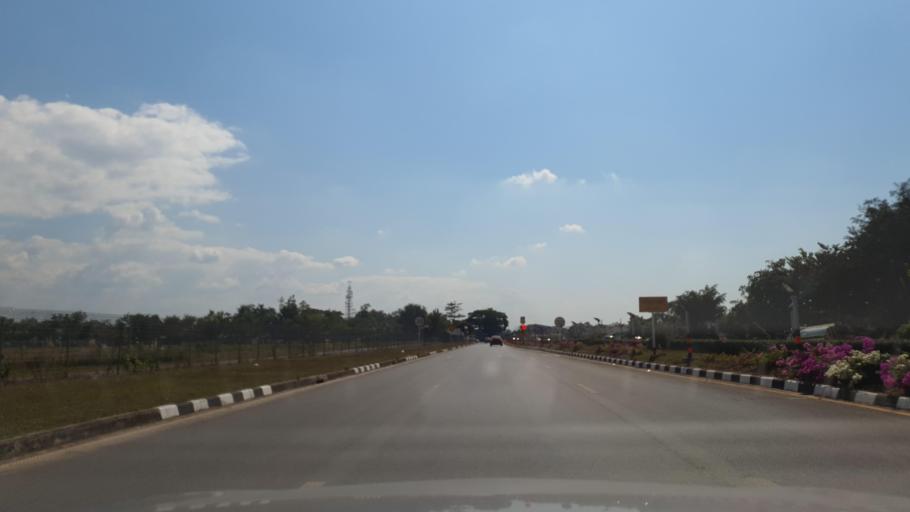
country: TH
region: Nan
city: Nan
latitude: 18.7989
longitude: 100.7788
